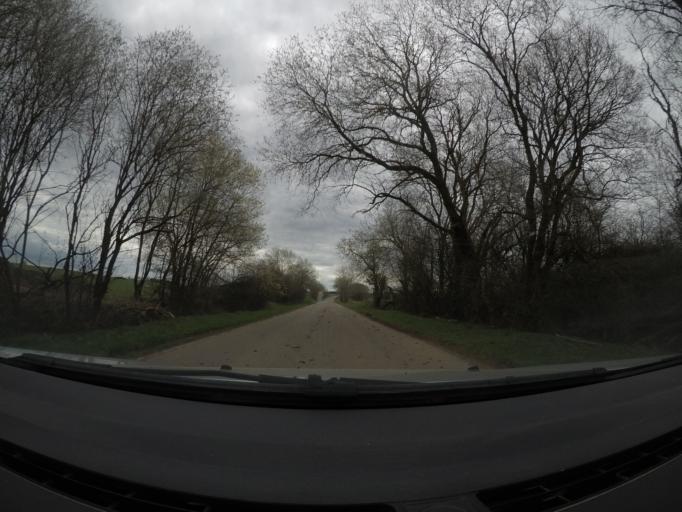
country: BE
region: Wallonia
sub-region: Province du Luxembourg
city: Leglise
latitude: 49.7743
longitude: 5.5414
